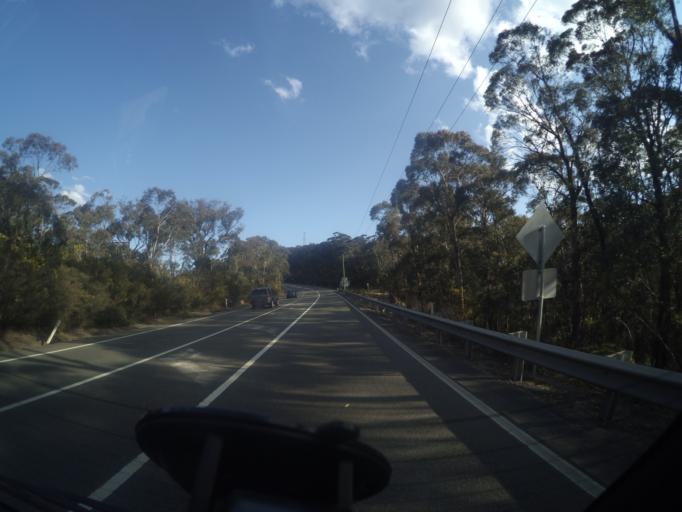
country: AU
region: New South Wales
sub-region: Blue Mountains Municipality
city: Katoomba
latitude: -33.6993
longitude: 150.2908
